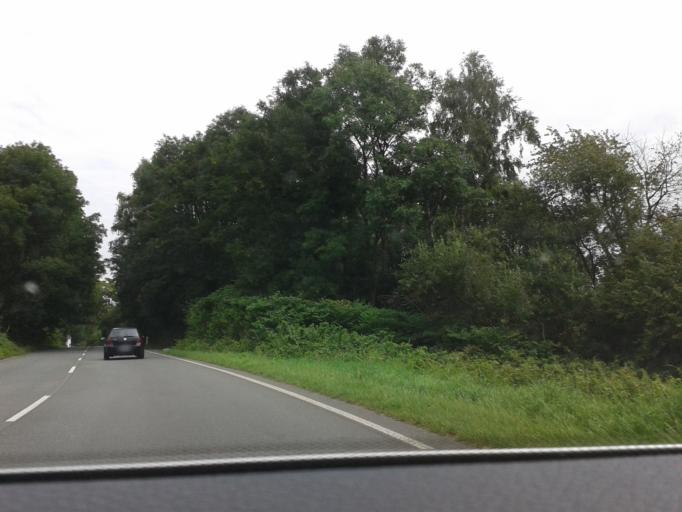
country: DE
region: North Rhine-Westphalia
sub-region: Regierungsbezirk Dusseldorf
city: Muelheim (Ruhr)
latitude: 51.4285
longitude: 6.9180
